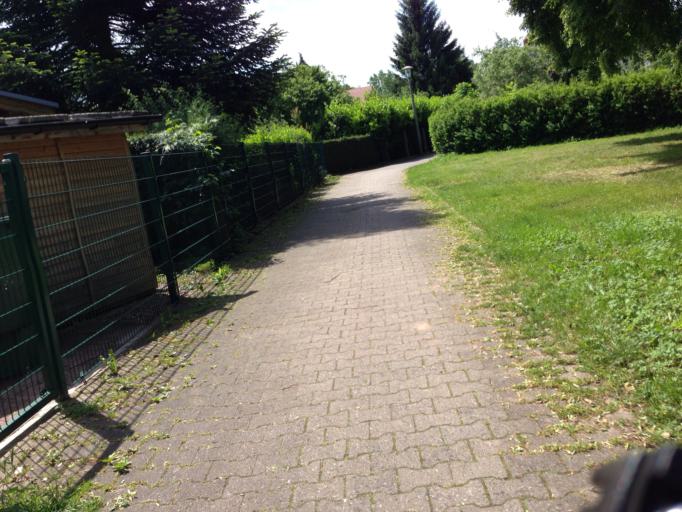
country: DE
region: Hesse
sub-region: Regierungsbezirk Darmstadt
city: Langenselbold
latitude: 50.1814
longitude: 9.0406
